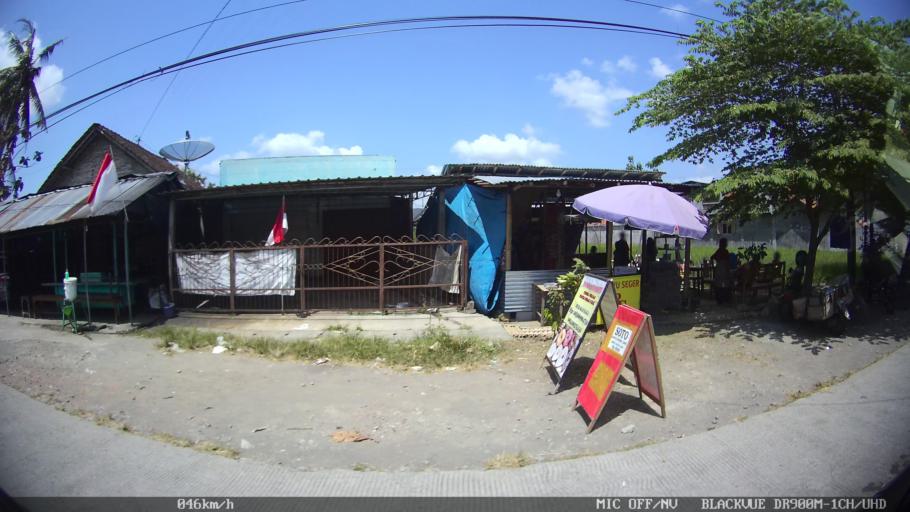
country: ID
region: Daerah Istimewa Yogyakarta
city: Pundong
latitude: -7.9229
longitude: 110.3747
